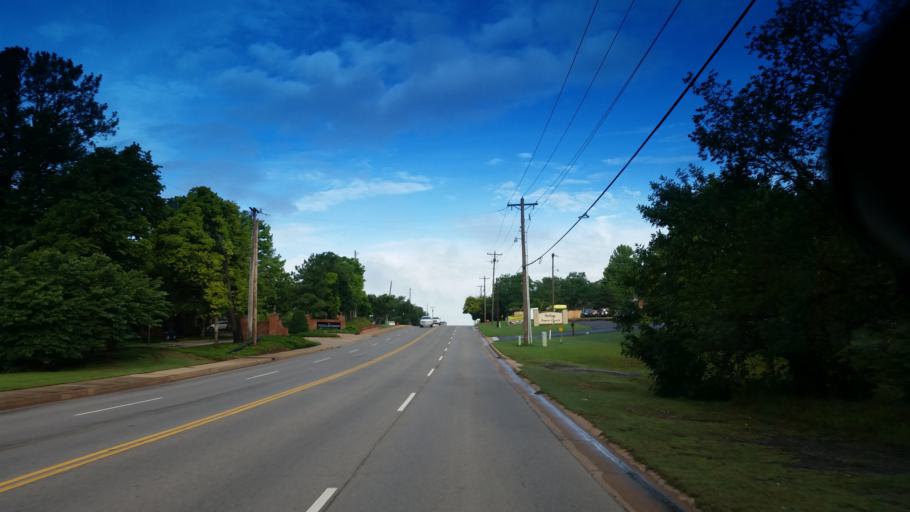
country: US
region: Oklahoma
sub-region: Oklahoma County
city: Edmond
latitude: 35.6383
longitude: -97.4536
